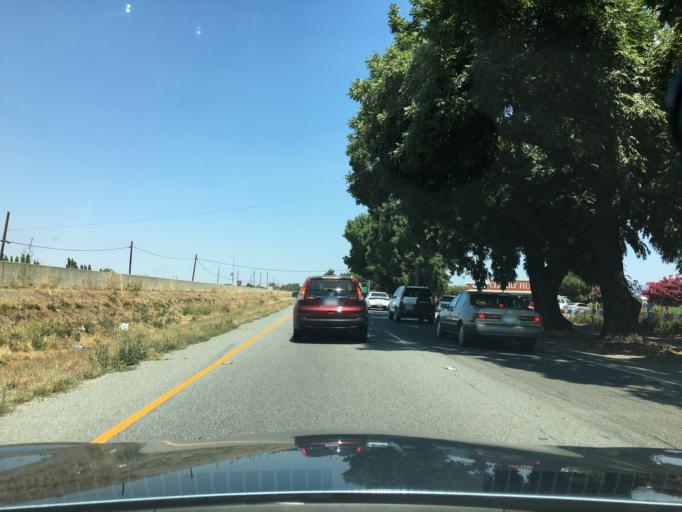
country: US
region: California
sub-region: Santa Clara County
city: Gilroy
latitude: 36.9650
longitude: -121.5519
